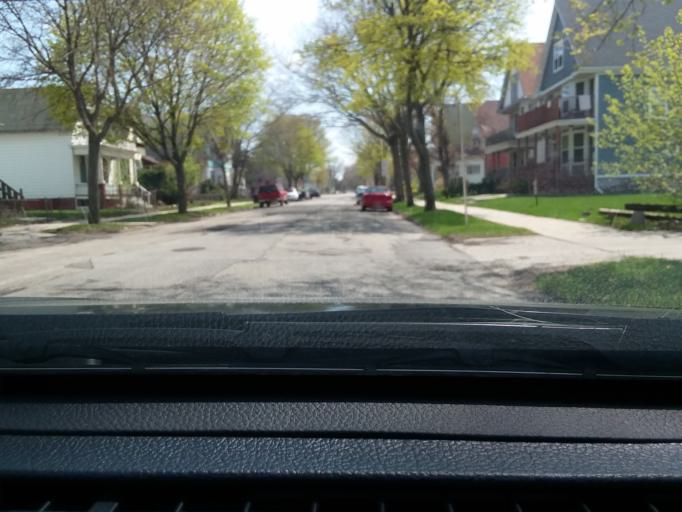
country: US
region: Wisconsin
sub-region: Milwaukee County
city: Milwaukee
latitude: 43.0691
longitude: -87.9241
